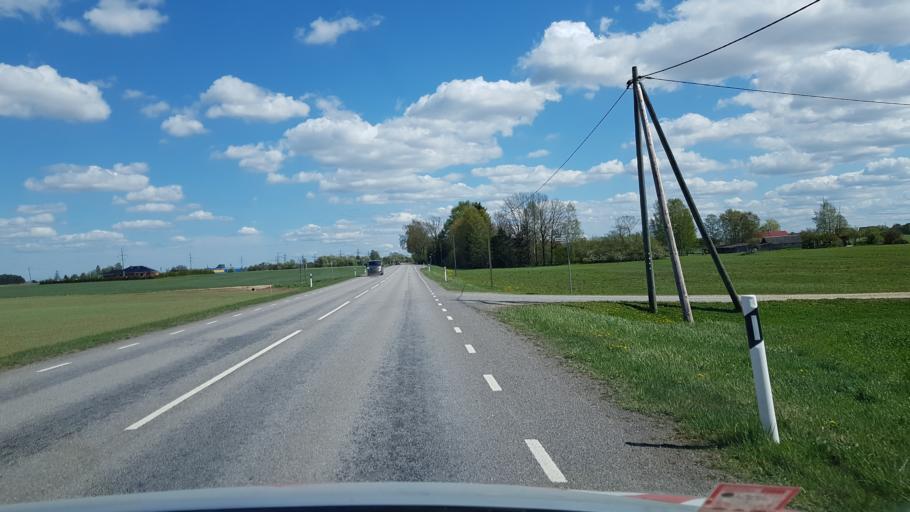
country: EE
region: Tartu
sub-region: Tartu linn
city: Tartu
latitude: 58.3799
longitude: 26.6520
